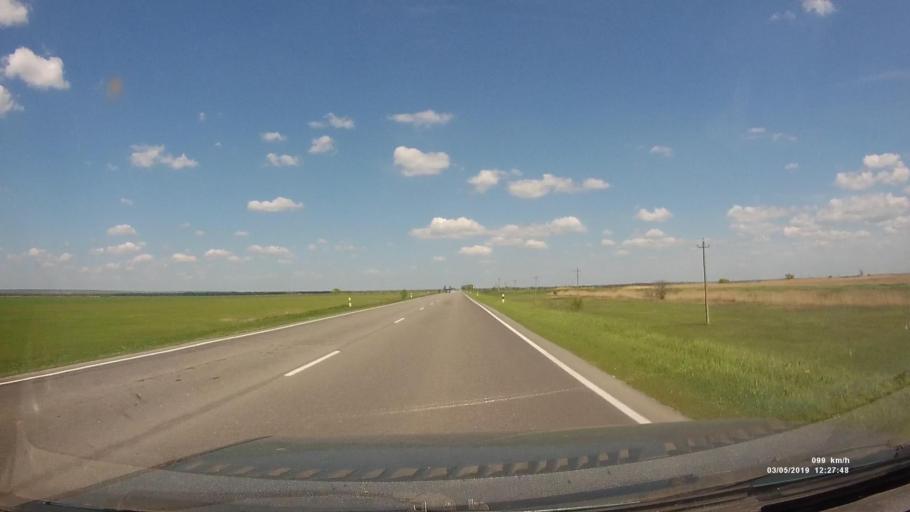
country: RU
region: Rostov
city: Semikarakorsk
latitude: 47.4638
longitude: 40.7233
